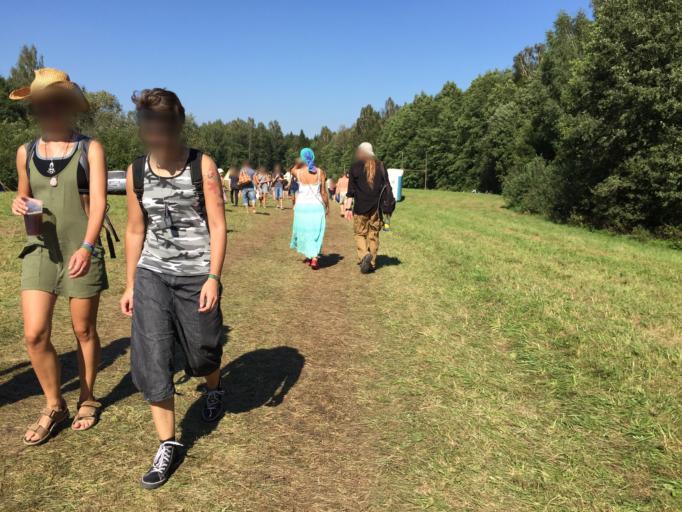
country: LT
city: Zarasai
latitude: 55.7889
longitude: 25.9626
